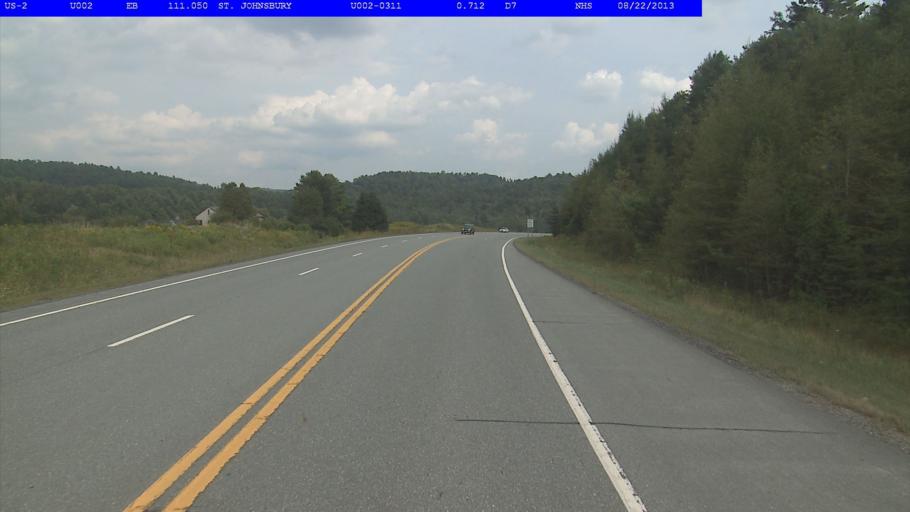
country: US
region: Vermont
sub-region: Caledonia County
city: St Johnsbury
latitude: 44.4429
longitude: -72.0471
